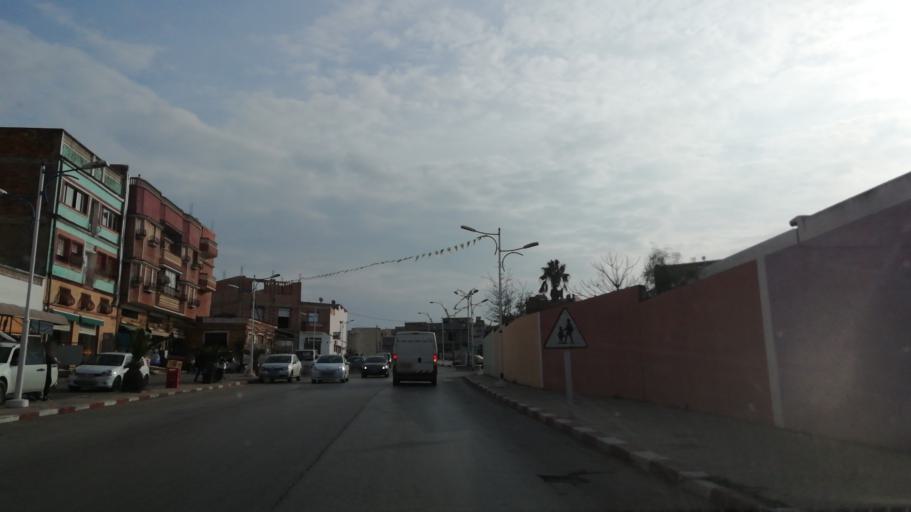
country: DZ
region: Mostaganem
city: Mostaganem
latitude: 35.8981
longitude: 0.0739
